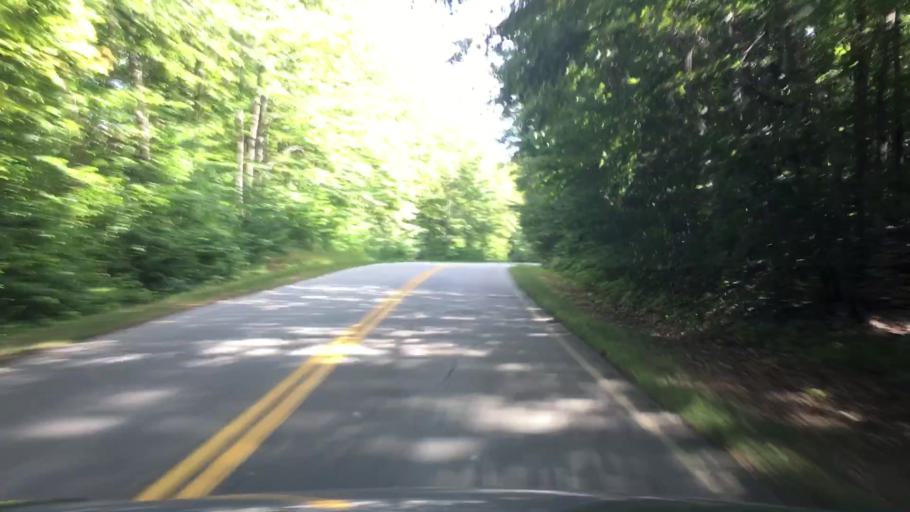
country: US
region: New Hampshire
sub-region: Carroll County
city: Tamworth
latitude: 44.0311
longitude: -71.3232
